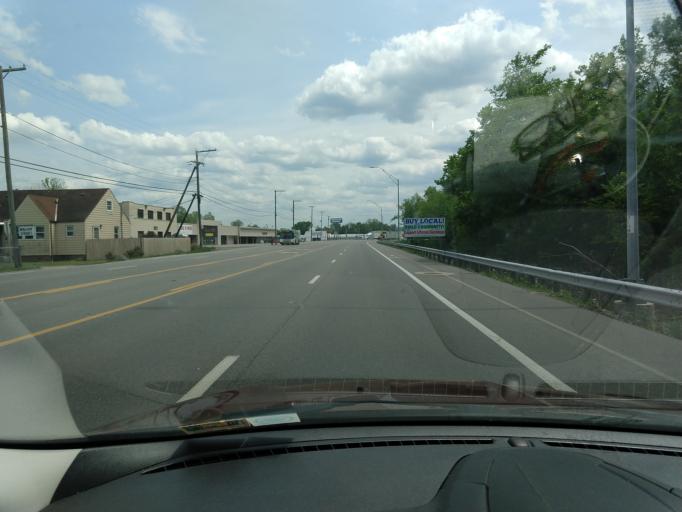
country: US
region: West Virginia
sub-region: Kanawha County
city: Dunbar
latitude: 38.3706
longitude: -81.7691
